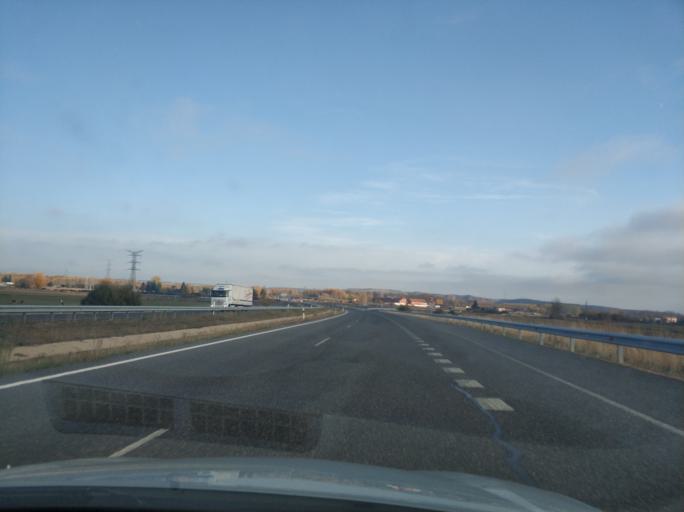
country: ES
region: Castille and Leon
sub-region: Provincia de Leon
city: Villaturiel
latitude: 42.5541
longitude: -5.4645
